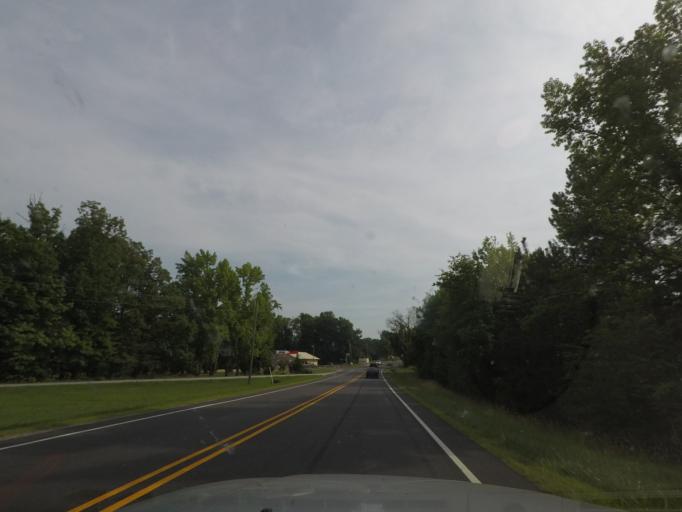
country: US
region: Virginia
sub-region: Prince Edward County
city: Hampden Sydney
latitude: 37.1262
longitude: -78.4511
